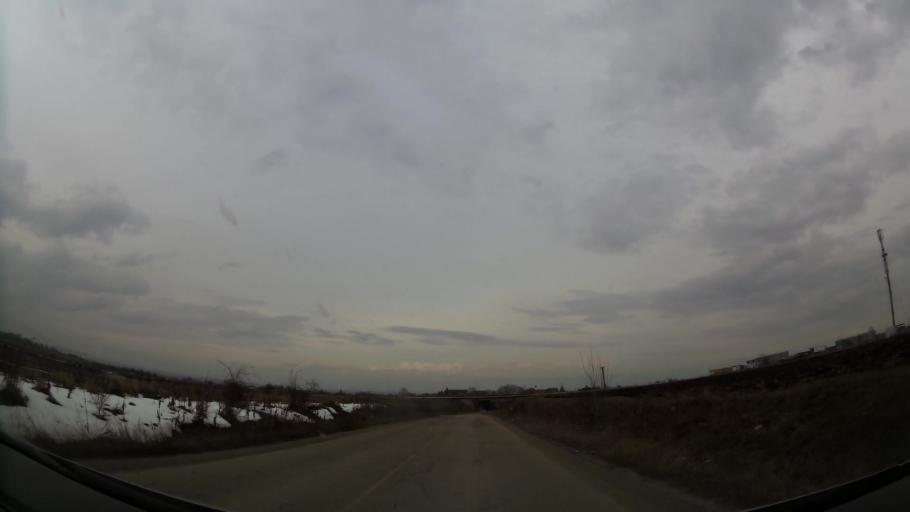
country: BG
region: Sofiya
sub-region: Obshtina Bozhurishte
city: Bozhurishte
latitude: 42.7125
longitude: 23.2197
